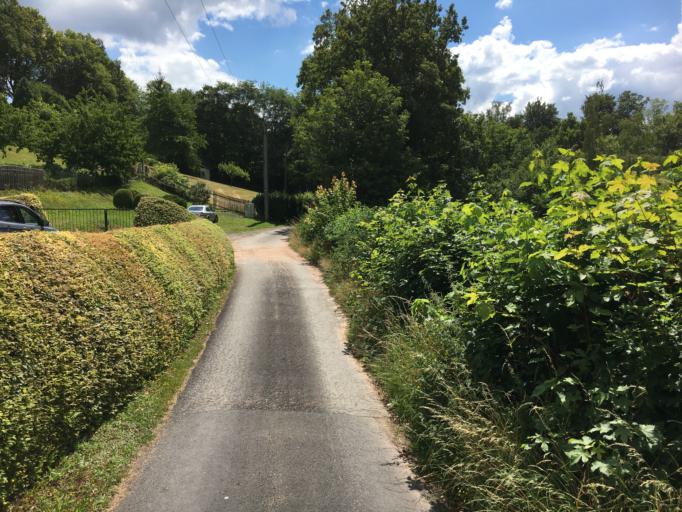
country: DE
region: Thuringia
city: Schmalkalden
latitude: 50.7258
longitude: 10.4599
